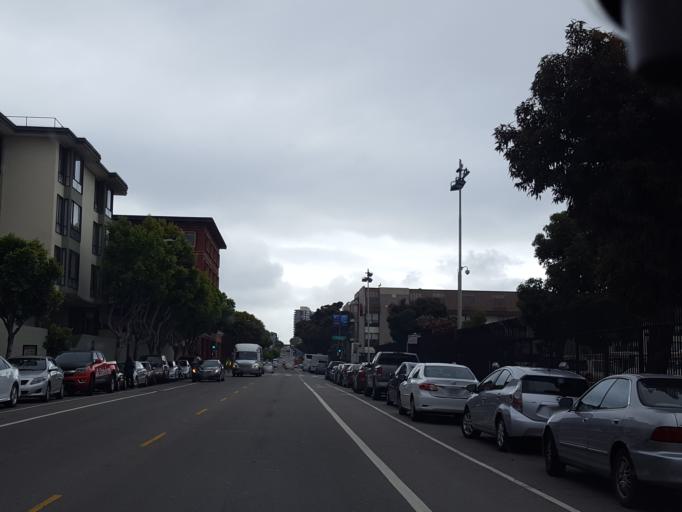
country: US
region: California
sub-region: San Francisco County
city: San Francisco
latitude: 37.8069
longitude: -122.4109
